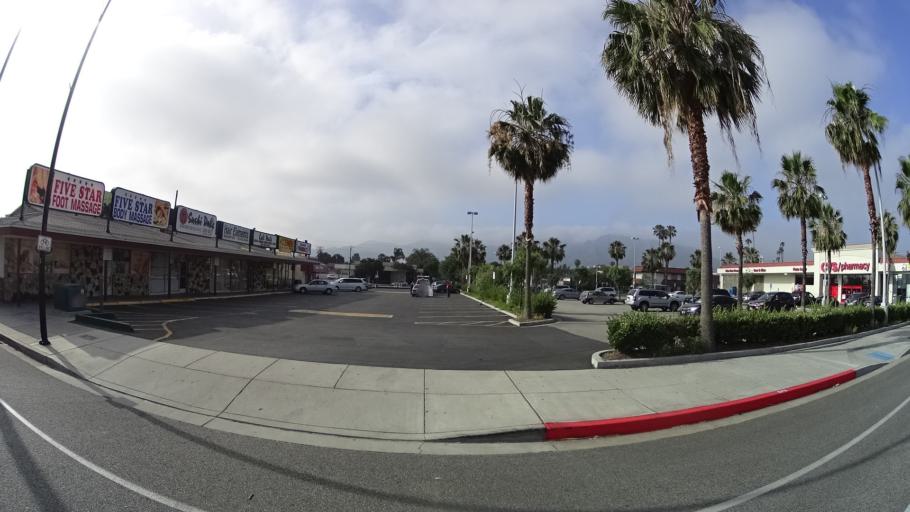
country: US
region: California
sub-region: Los Angeles County
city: Burbank
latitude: 34.1675
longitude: -118.3243
